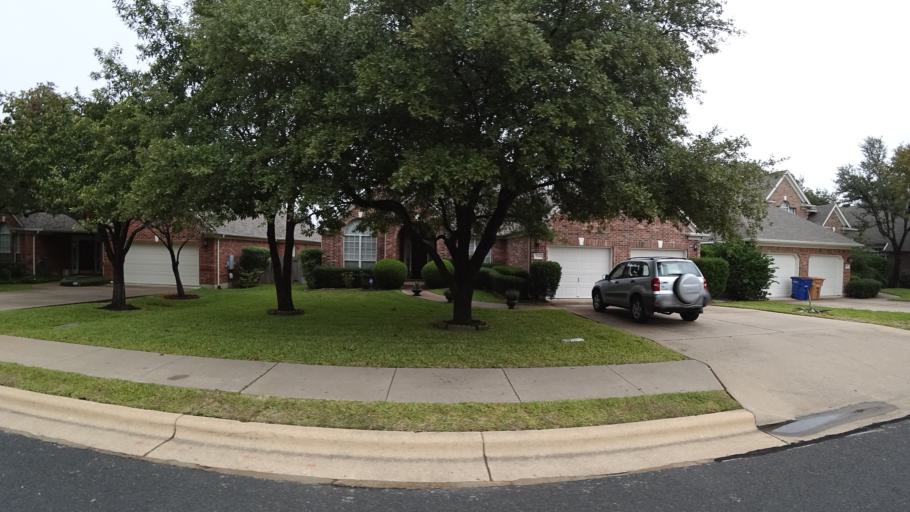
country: US
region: Texas
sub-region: Travis County
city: Shady Hollow
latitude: 30.1952
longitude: -97.8739
